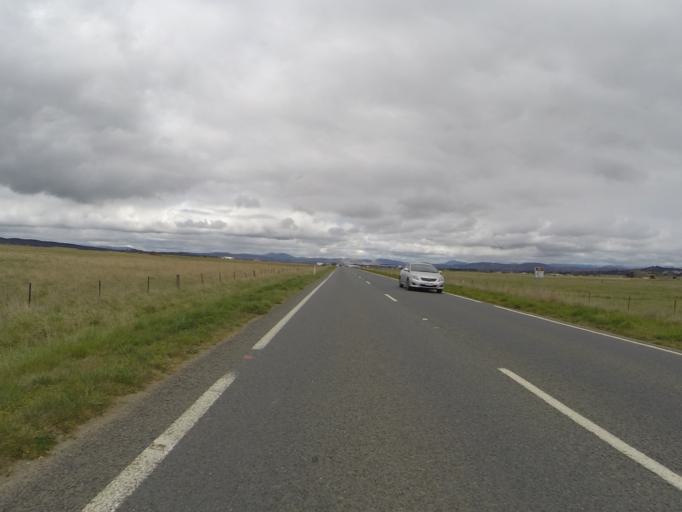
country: AU
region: Australian Capital Territory
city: Canberra
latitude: -35.2742
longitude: 149.1952
